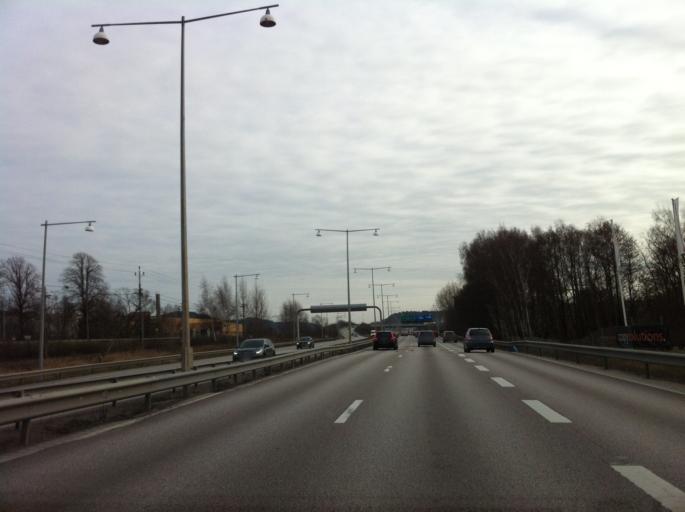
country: SE
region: Vaestra Goetaland
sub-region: Goteborg
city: Goeteborg
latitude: 57.7035
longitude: 11.9948
